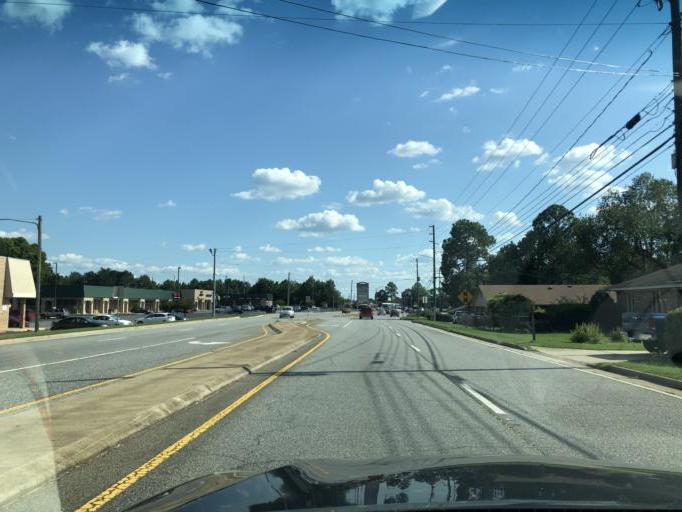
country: US
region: Georgia
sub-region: Muscogee County
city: Columbus
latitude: 32.5300
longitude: -84.9251
